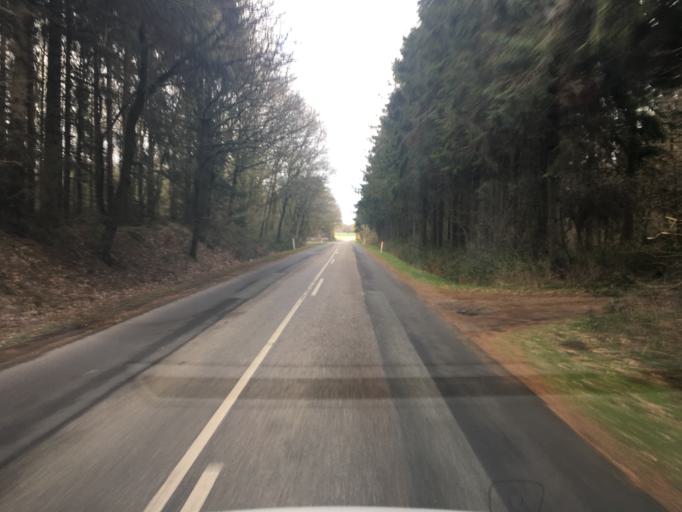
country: DK
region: South Denmark
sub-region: Aabenraa Kommune
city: Krusa
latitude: 54.8982
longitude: 9.4733
